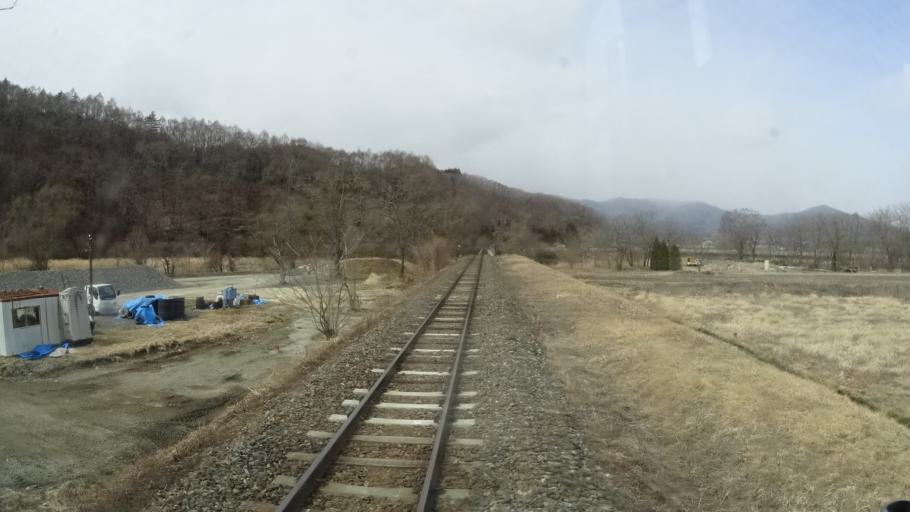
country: JP
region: Iwate
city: Tono
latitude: 39.3257
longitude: 141.5535
